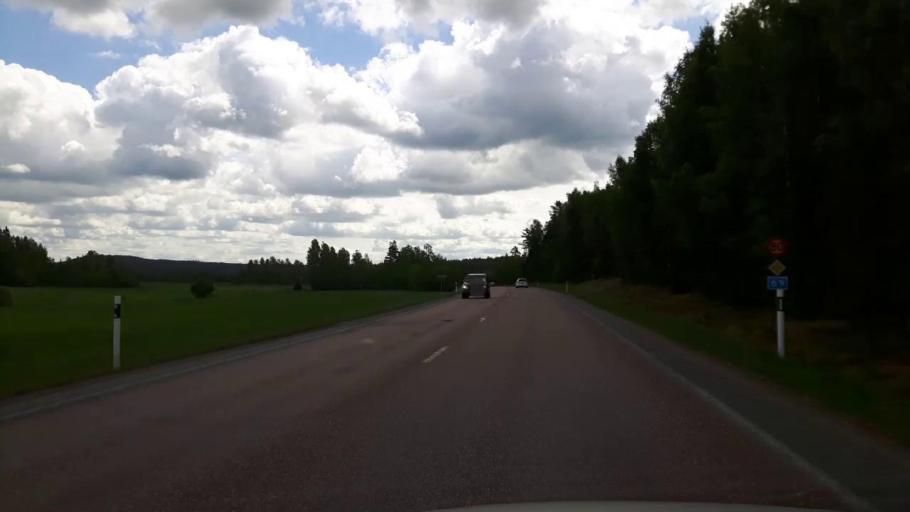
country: SE
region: Dalarna
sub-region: Faluns Kommun
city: Falun
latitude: 60.5059
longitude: 15.7394
